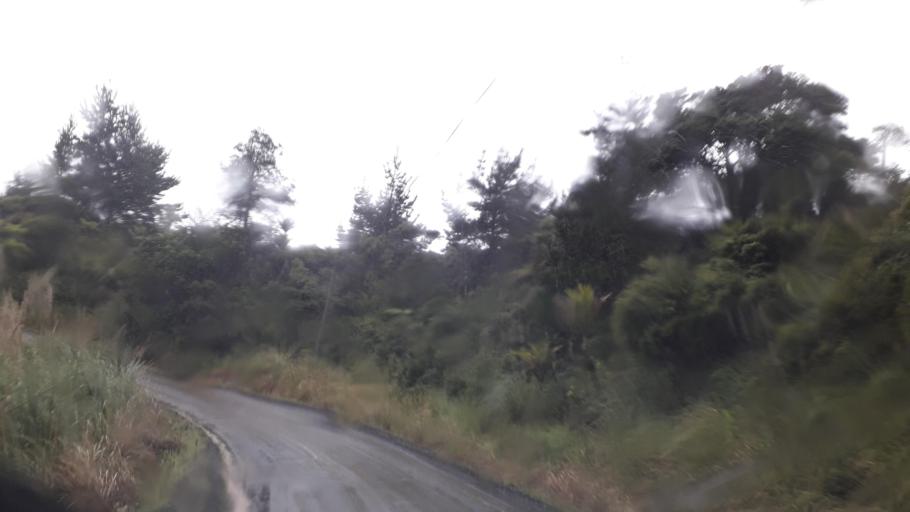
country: NZ
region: Northland
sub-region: Far North District
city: Kaitaia
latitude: -35.3692
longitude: 173.4121
